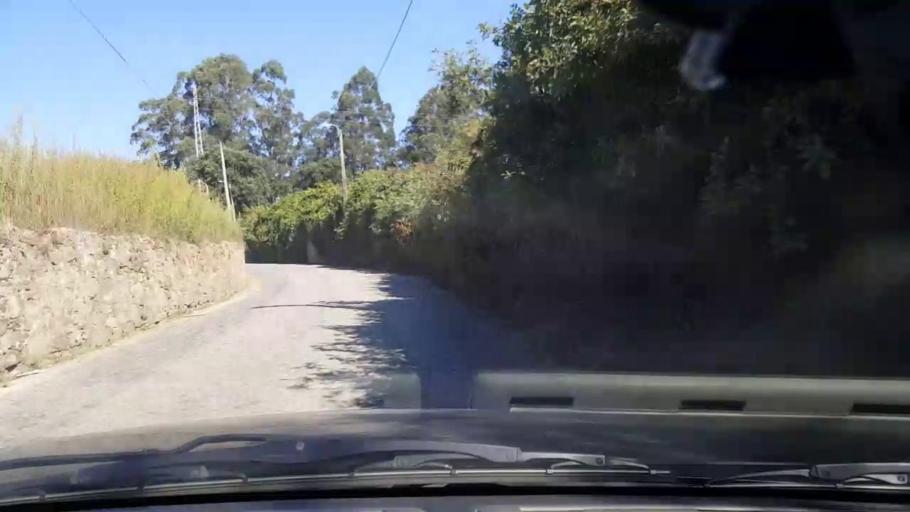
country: PT
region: Porto
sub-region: Maia
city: Gemunde
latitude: 41.2827
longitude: -8.6722
